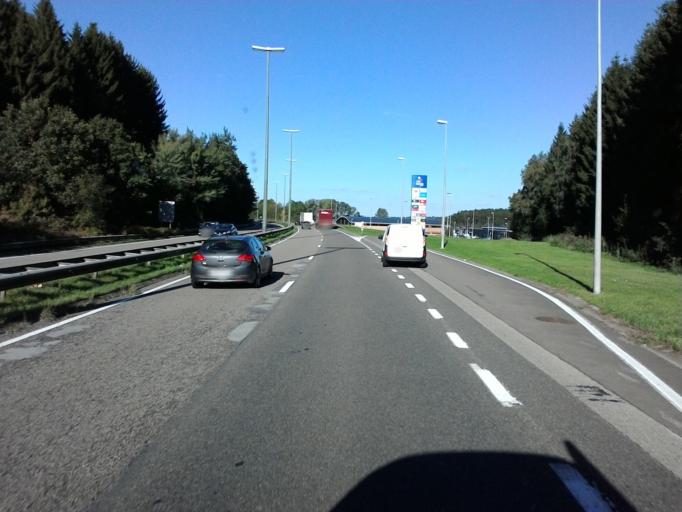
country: BE
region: Wallonia
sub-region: Province du Luxembourg
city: Arlon
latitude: 49.6807
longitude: 5.7854
